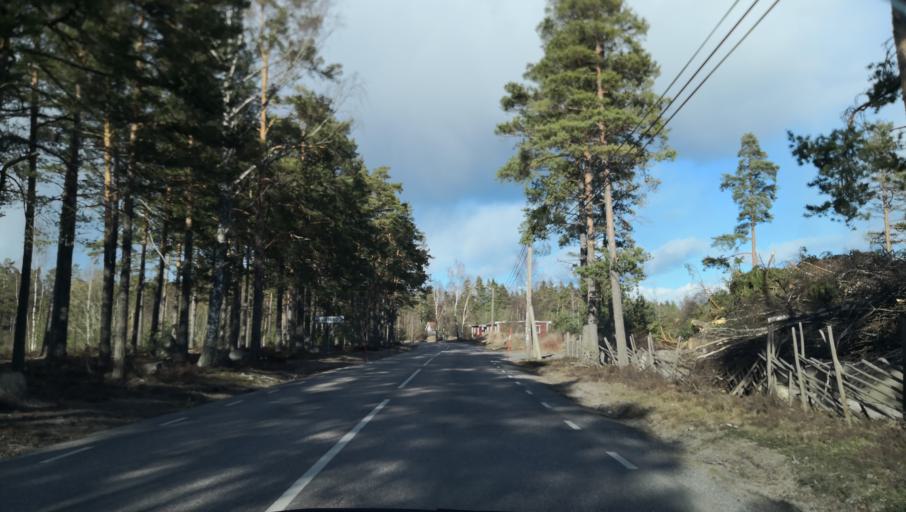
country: SE
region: Stockholm
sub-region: Varmdo Kommun
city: Mortnas
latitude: 59.2754
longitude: 18.4720
